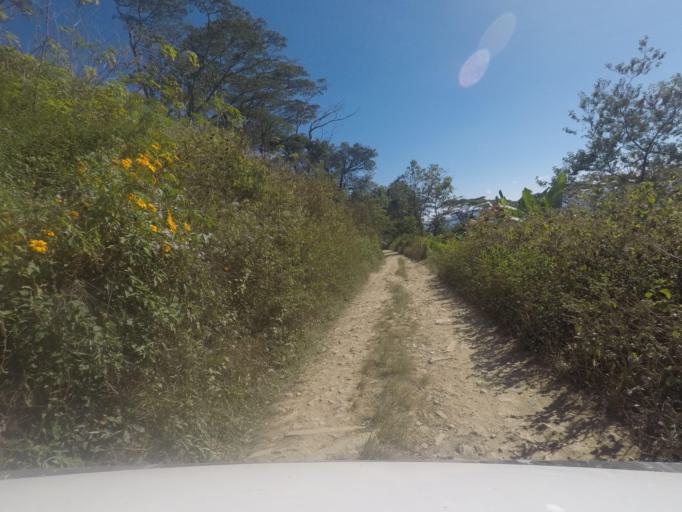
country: TL
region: Ermera
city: Gleno
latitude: -8.7360
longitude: 125.3437
